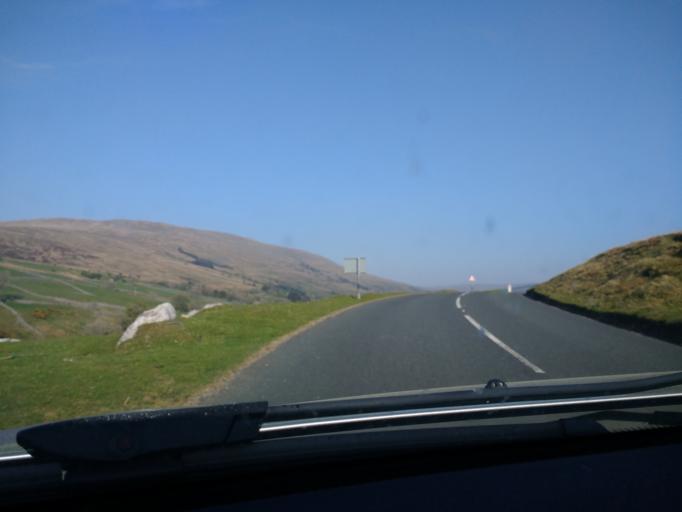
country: GB
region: England
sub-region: Cumbria
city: Sedbergh
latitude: 54.3152
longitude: -2.4689
